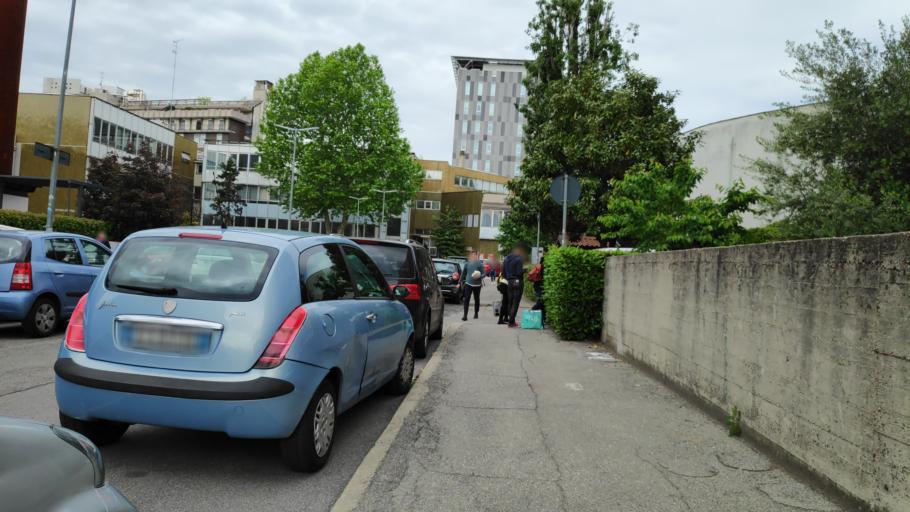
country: IT
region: Lombardy
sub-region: Citta metropolitana di Milano
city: Milano
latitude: 45.4761
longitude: 9.2338
